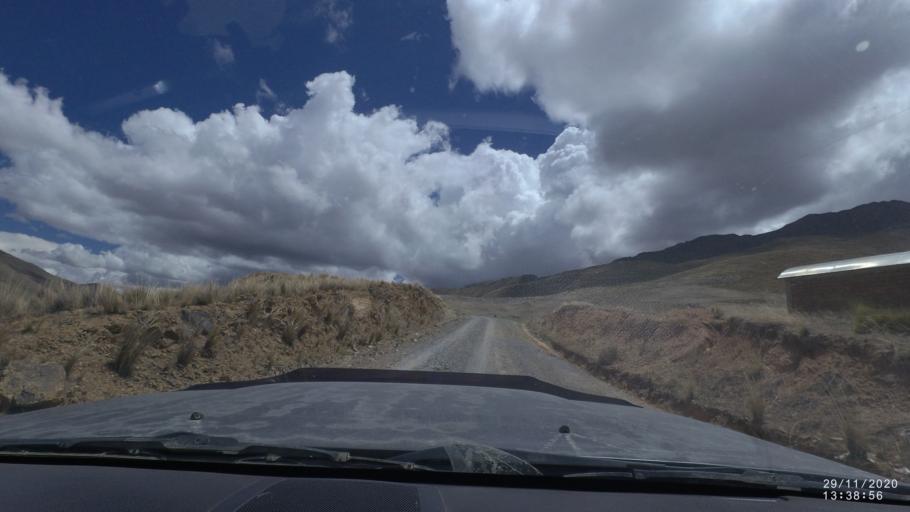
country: BO
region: Cochabamba
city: Cochabamba
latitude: -17.1212
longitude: -66.3276
